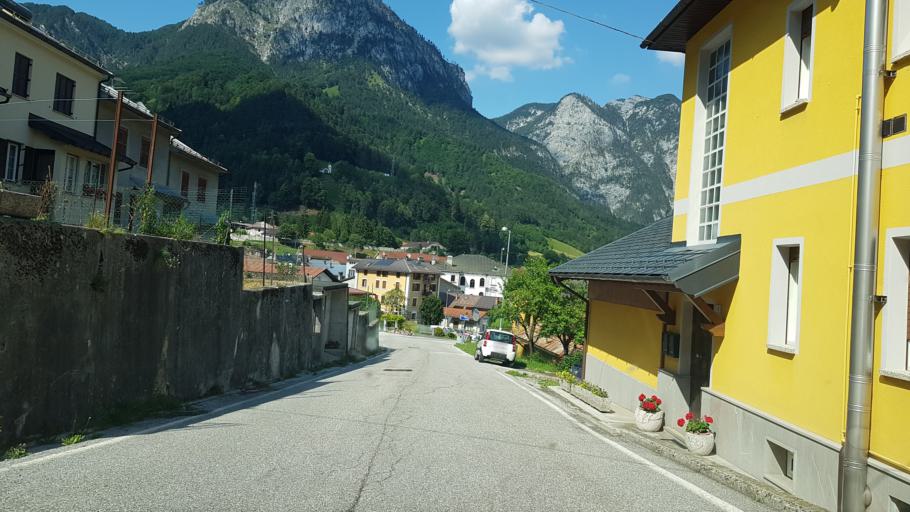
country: IT
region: Friuli Venezia Giulia
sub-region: Provincia di Udine
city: Pontebba
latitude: 46.5047
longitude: 13.3025
